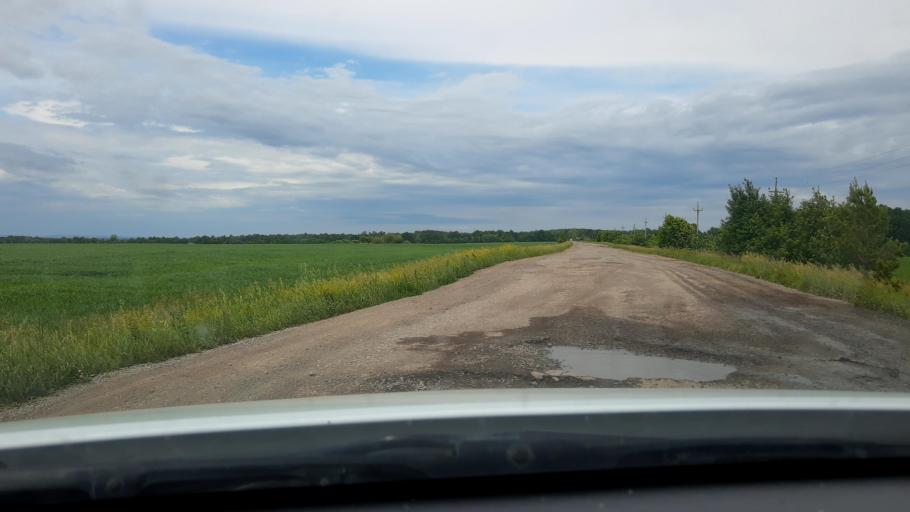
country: RU
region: Bashkortostan
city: Iglino
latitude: 54.7526
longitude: 56.5292
